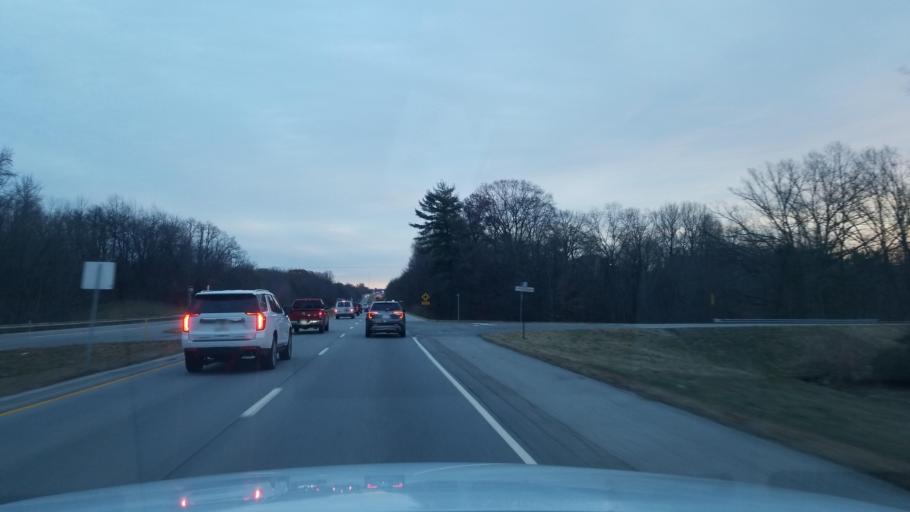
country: US
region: Indiana
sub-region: Vanderburgh County
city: Evansville
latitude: 37.9704
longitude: -87.6614
